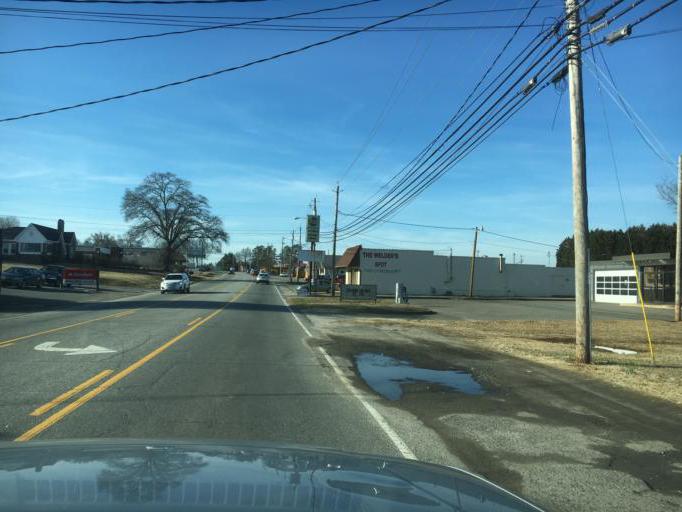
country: US
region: North Carolina
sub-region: Rutherford County
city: Forest City
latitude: 35.3461
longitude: -81.8850
